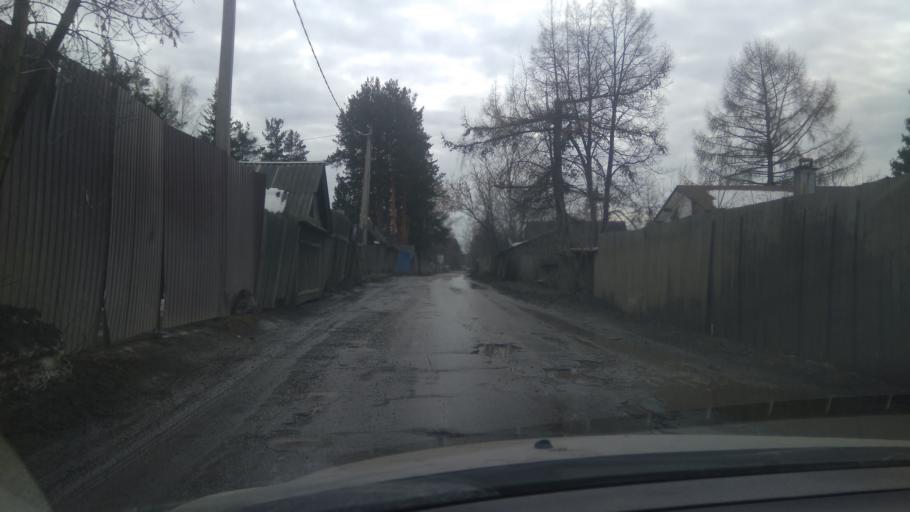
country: RU
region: Sverdlovsk
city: Severka
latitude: 56.8505
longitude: 60.3851
